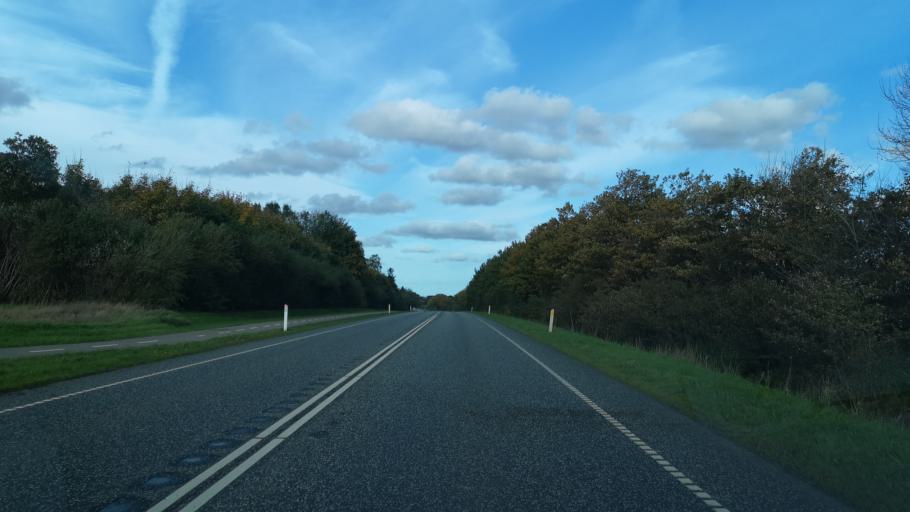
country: DK
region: Central Jutland
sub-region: Holstebro Kommune
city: Holstebro
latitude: 56.3239
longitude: 8.6098
